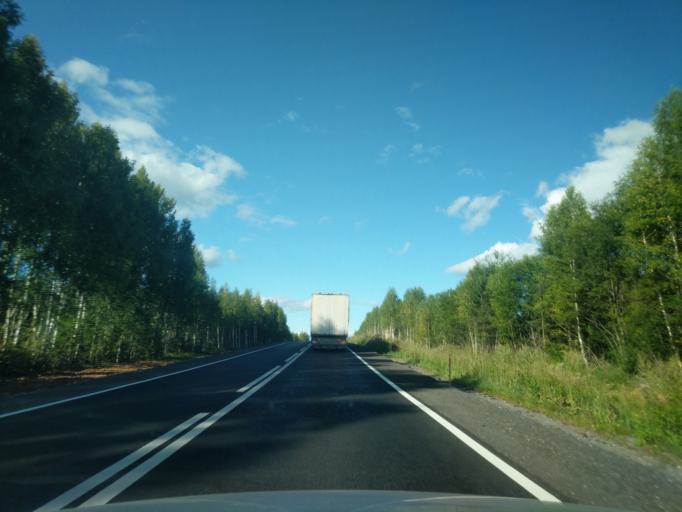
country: RU
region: Kostroma
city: Makar'yev
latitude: 57.9922
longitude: 43.9687
